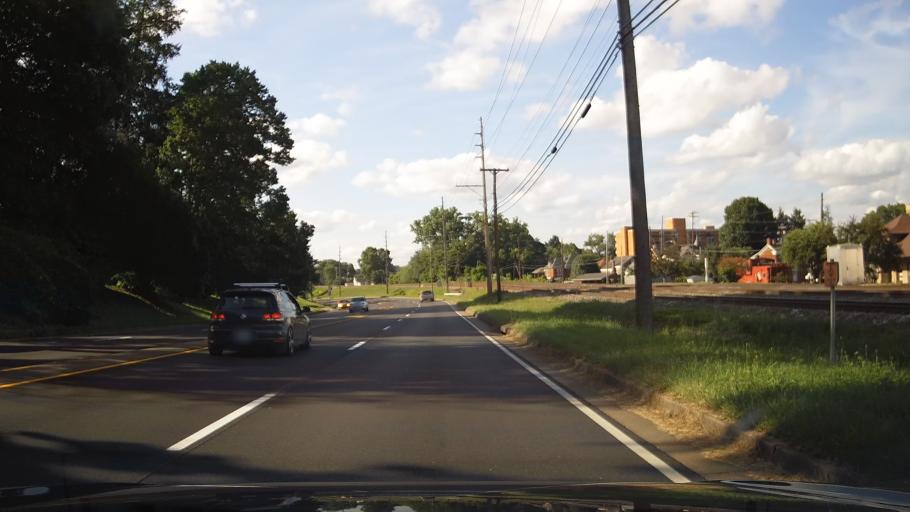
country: US
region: Kentucky
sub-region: Boyd County
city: Catlettsburg
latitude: 38.4164
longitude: -82.5998
